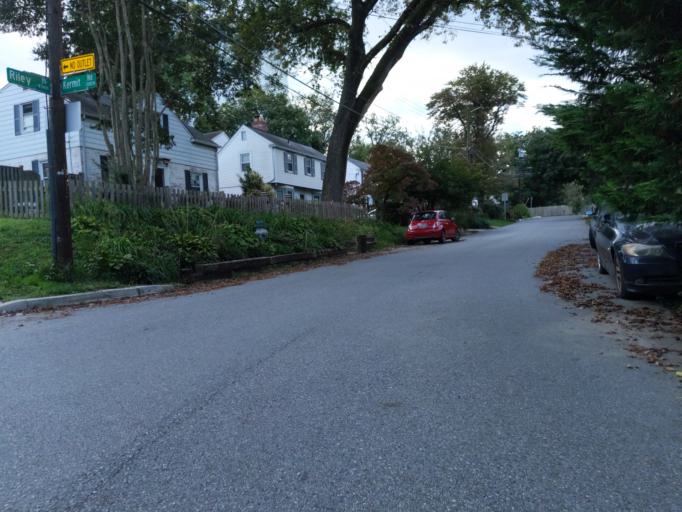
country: US
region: Maryland
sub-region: Montgomery County
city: Forest Glen
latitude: 39.0105
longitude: -77.0435
